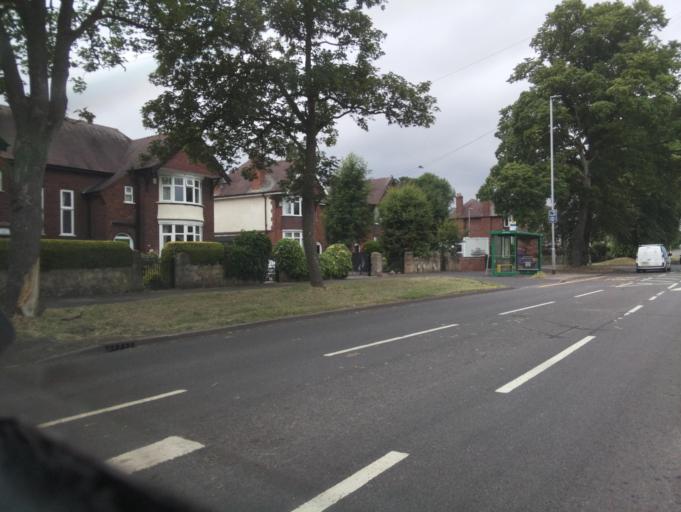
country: GB
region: England
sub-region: Staffordshire
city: Stafford
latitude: 52.7906
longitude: -2.1200
